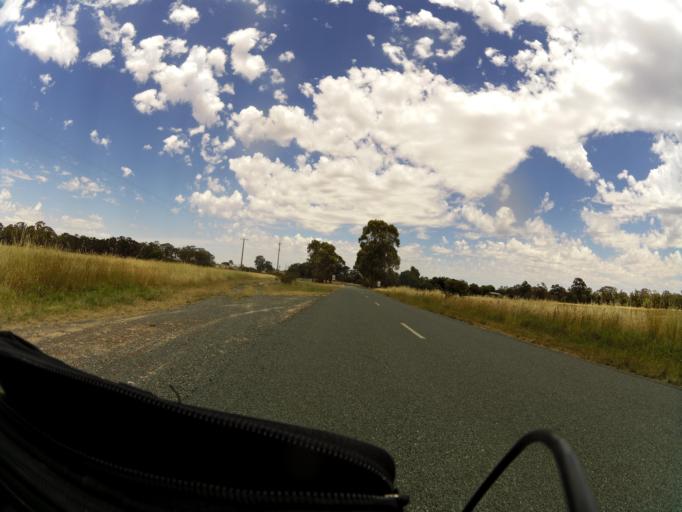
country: AU
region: Victoria
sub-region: Greater Shepparton
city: Shepparton
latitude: -36.6263
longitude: 145.2128
